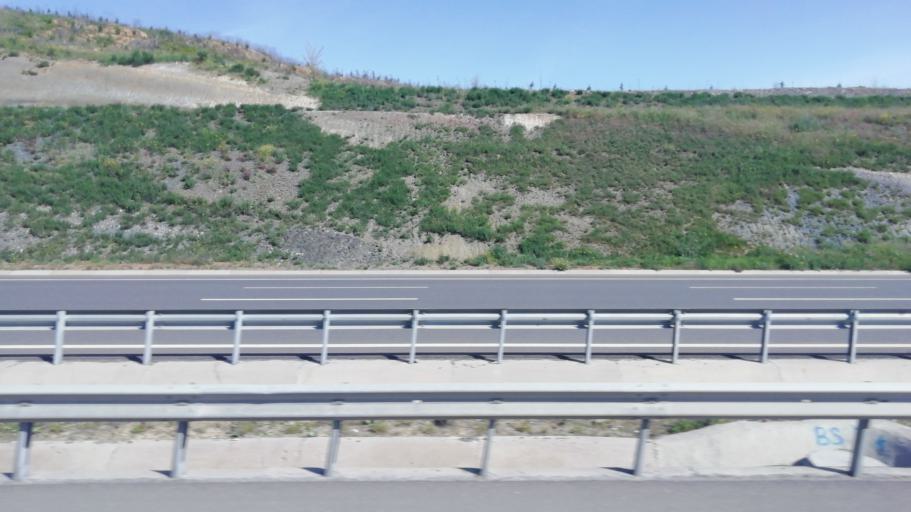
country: TR
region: Istanbul
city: Arikoey
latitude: 41.2264
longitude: 29.0516
